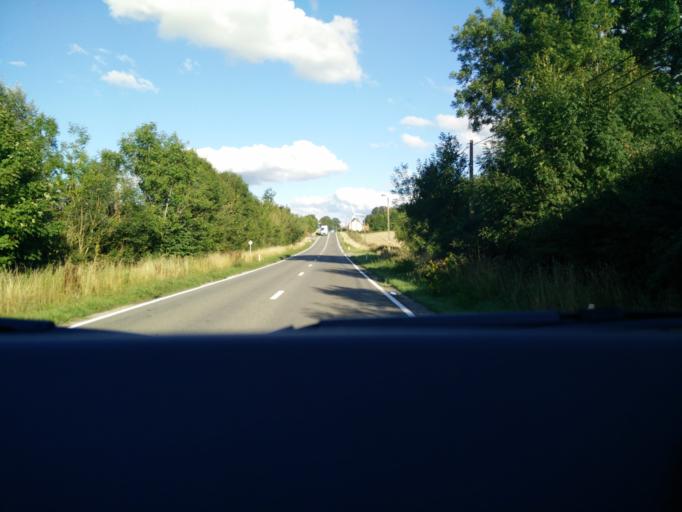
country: BE
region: Wallonia
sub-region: Province du Hainaut
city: Beaumont
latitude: 50.2282
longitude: 4.3062
